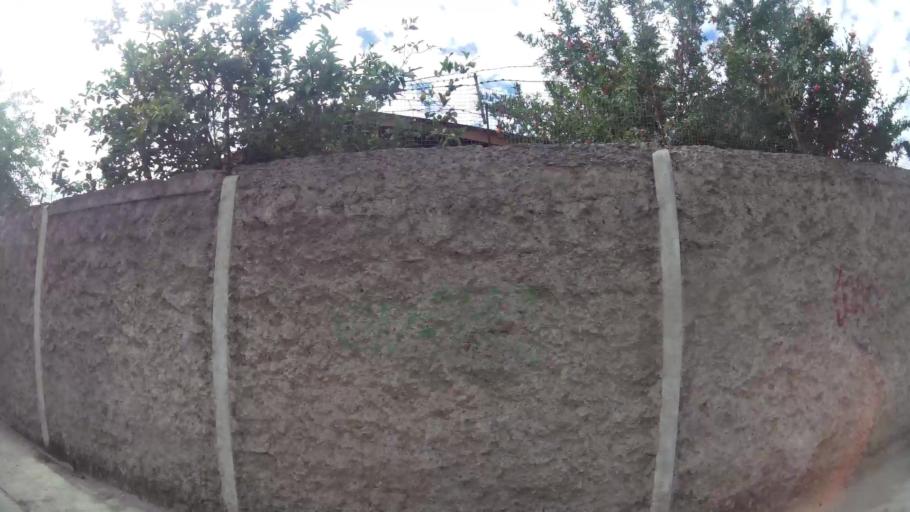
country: CL
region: Santiago Metropolitan
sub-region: Provincia de Santiago
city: La Pintana
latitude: -33.6206
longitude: -70.6194
